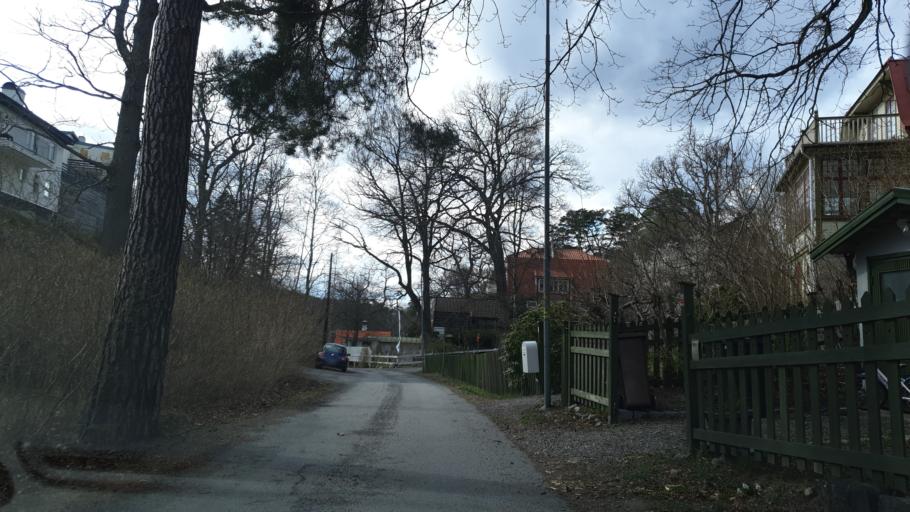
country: SE
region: Stockholm
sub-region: Nacka Kommun
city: Saltsjobaden
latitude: 59.2777
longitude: 18.3059
